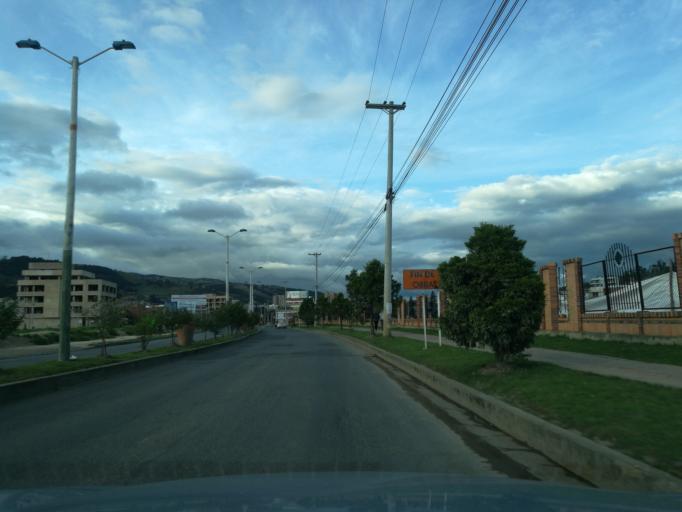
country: CO
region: Boyaca
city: Tunja
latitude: 5.5502
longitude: -73.3460
